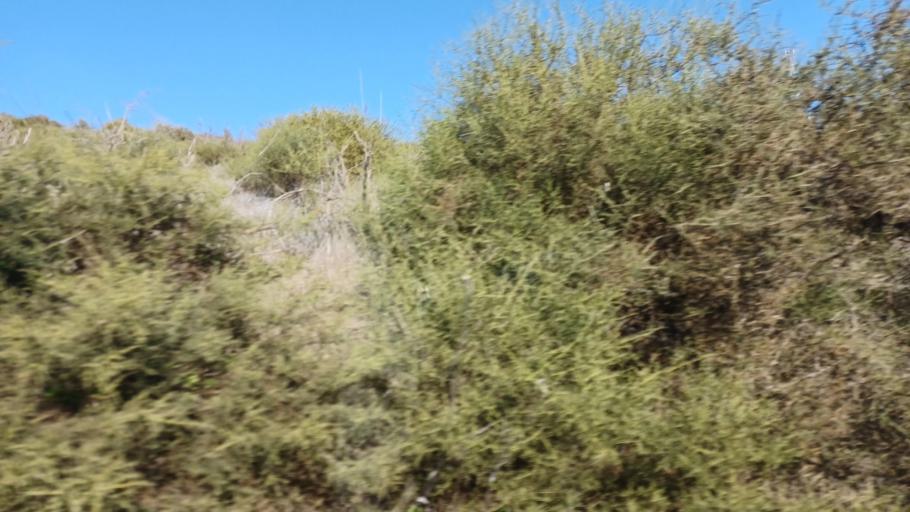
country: CY
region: Limassol
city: Pachna
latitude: 34.8096
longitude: 32.6672
